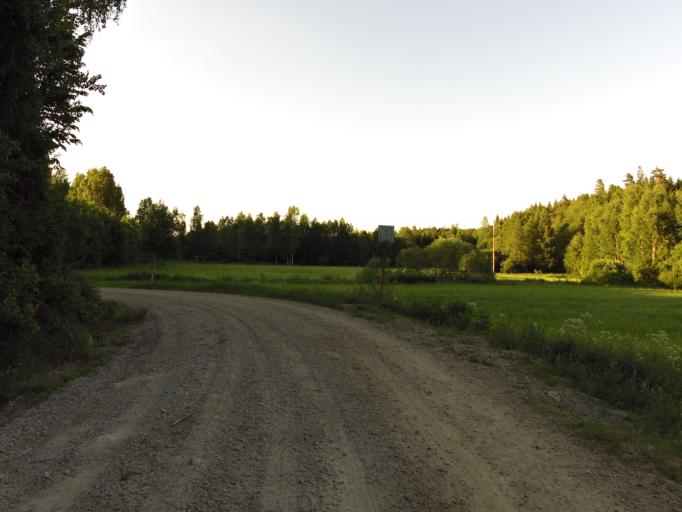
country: SE
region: Blekinge
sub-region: Olofstroms Kommun
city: Olofstroem
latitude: 56.4106
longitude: 14.5608
